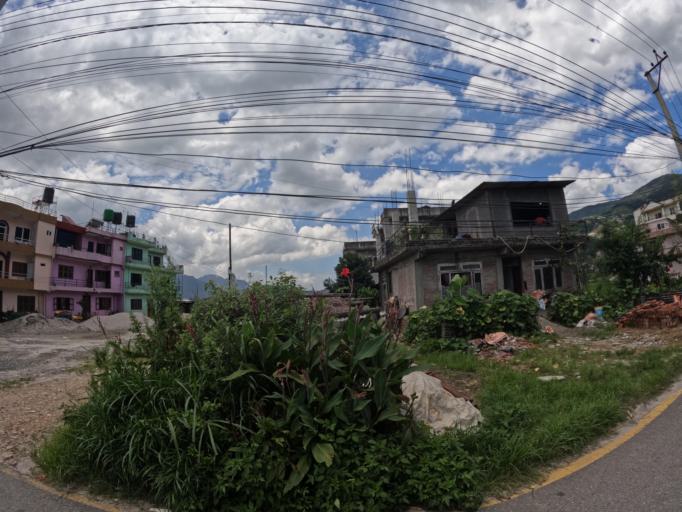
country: NP
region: Central Region
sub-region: Bagmati Zone
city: Kathmandu
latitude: 27.7807
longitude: 85.3251
